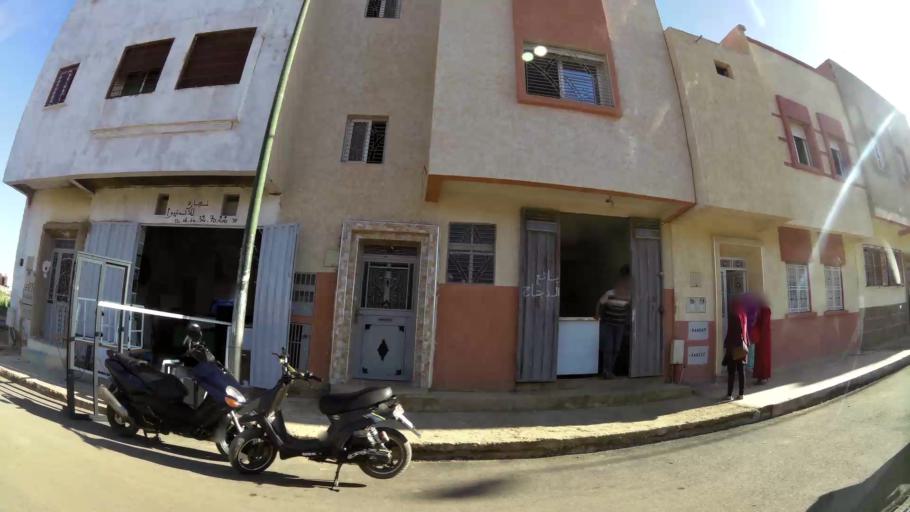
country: MA
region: Meknes-Tafilalet
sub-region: Meknes
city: Meknes
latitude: 33.8882
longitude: -5.5080
